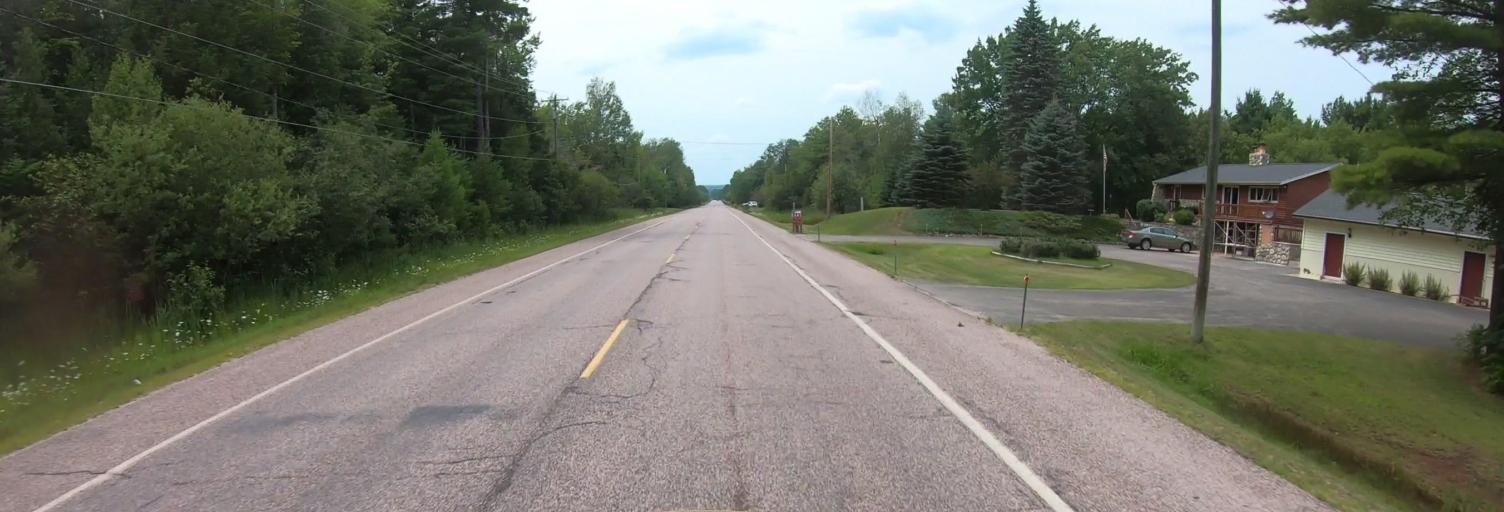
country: US
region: Michigan
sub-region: Marquette County
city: Harvey
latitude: 46.4636
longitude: -87.3289
